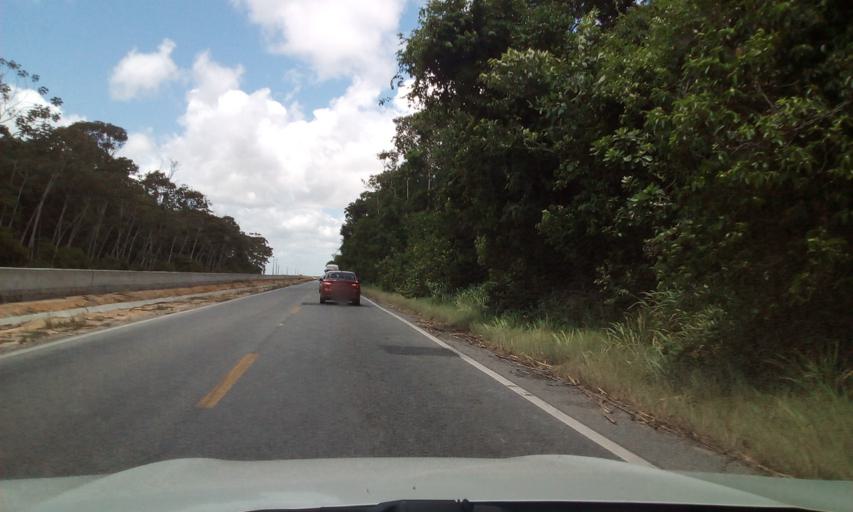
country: BR
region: Alagoas
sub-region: Pilar
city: Pilar
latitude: -9.6155
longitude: -36.0285
